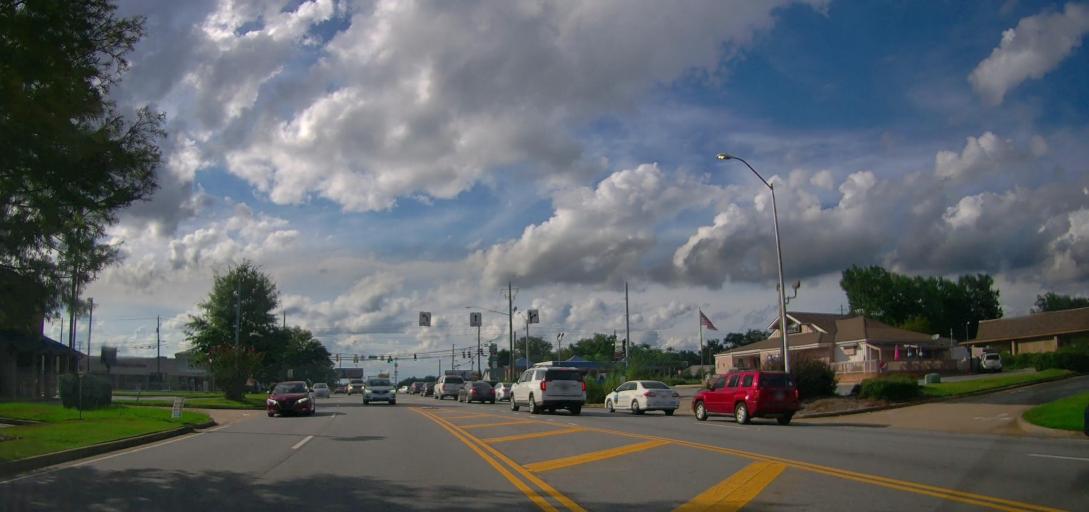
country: US
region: Alabama
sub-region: Russell County
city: Phenix City
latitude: 32.5254
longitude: -84.9608
